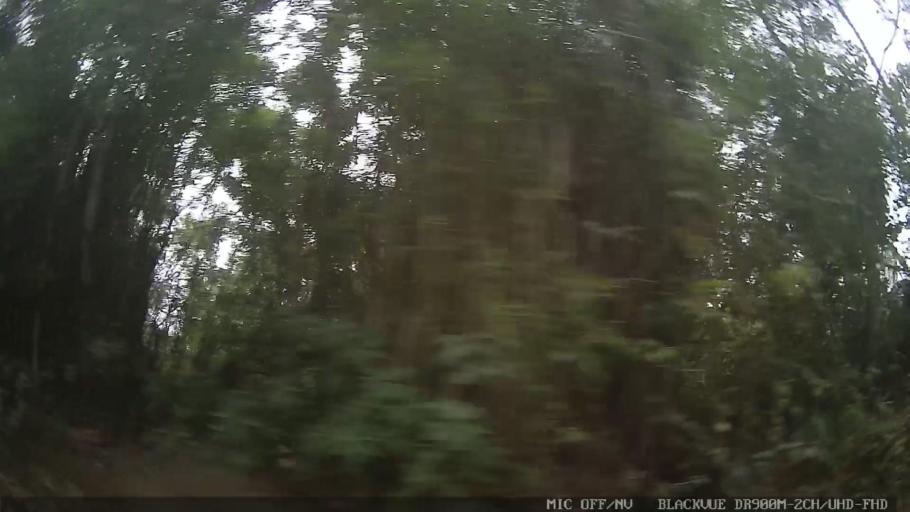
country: BR
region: Sao Paulo
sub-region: Suzano
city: Suzano
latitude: -23.6846
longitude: -46.2385
